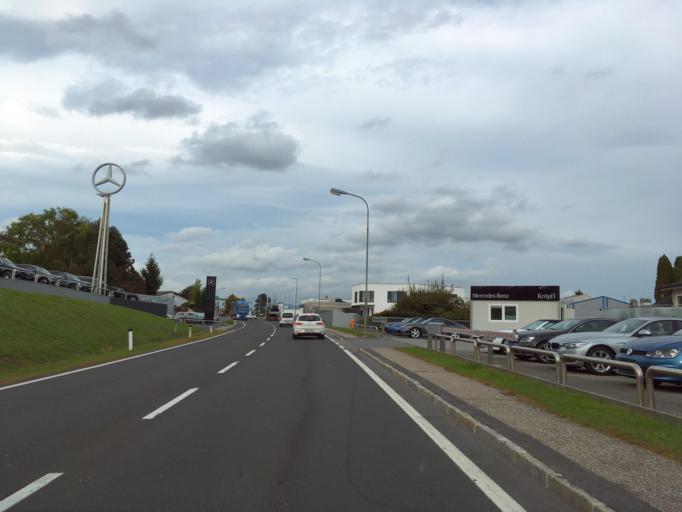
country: AT
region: Styria
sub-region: Politischer Bezirk Hartberg-Fuerstenfeld
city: Hartberg
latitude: 47.2854
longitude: 15.9786
